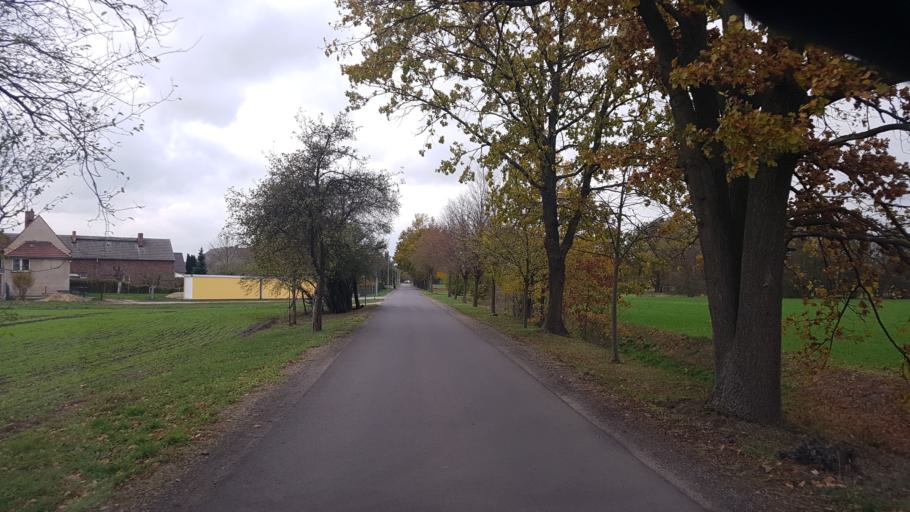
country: DE
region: Brandenburg
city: Schonewalde
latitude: 51.6555
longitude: 13.6063
